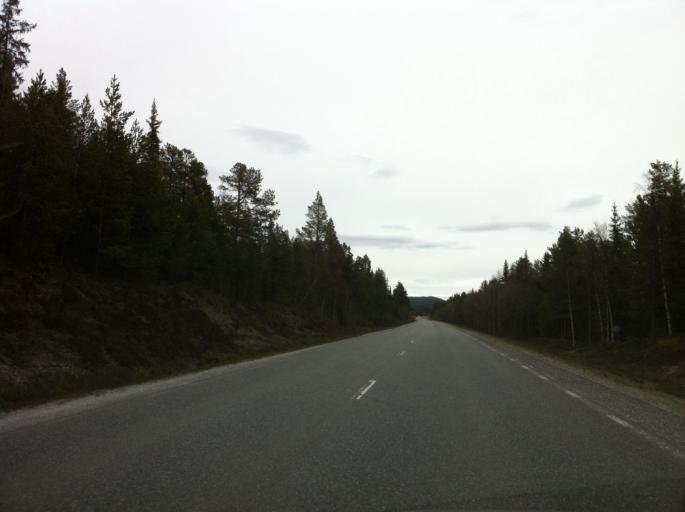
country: NO
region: Hedmark
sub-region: Engerdal
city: Engerdal
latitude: 62.5323
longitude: 12.5642
